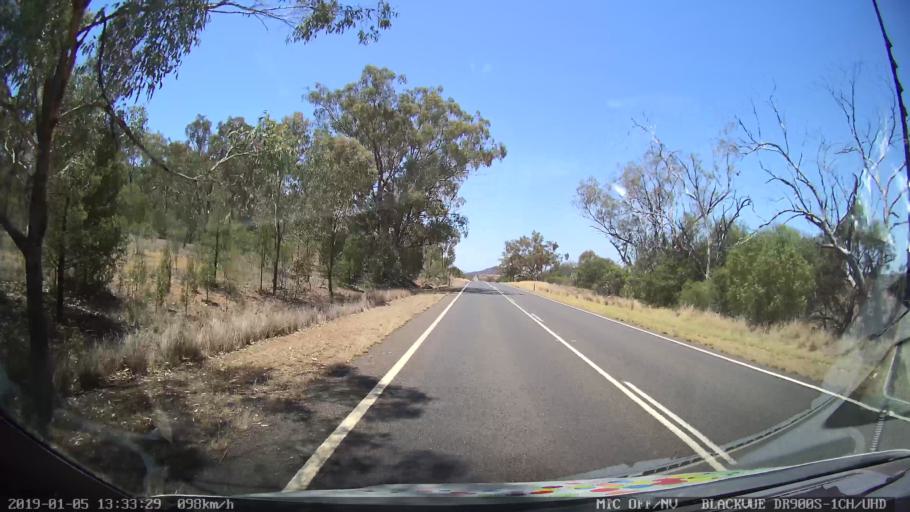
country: AU
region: New South Wales
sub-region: Gunnedah
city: Gunnedah
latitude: -31.0005
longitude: 150.1172
